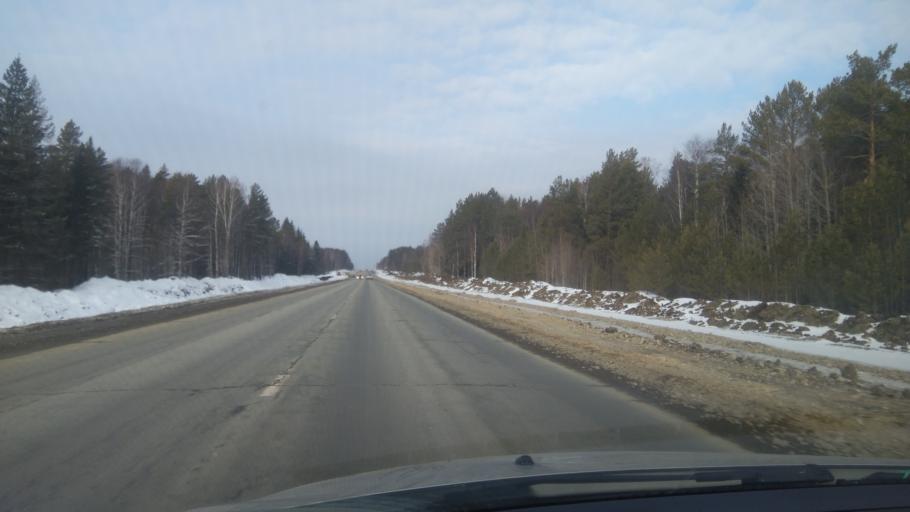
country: RU
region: Sverdlovsk
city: Bisert'
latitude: 56.8297
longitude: 58.9665
